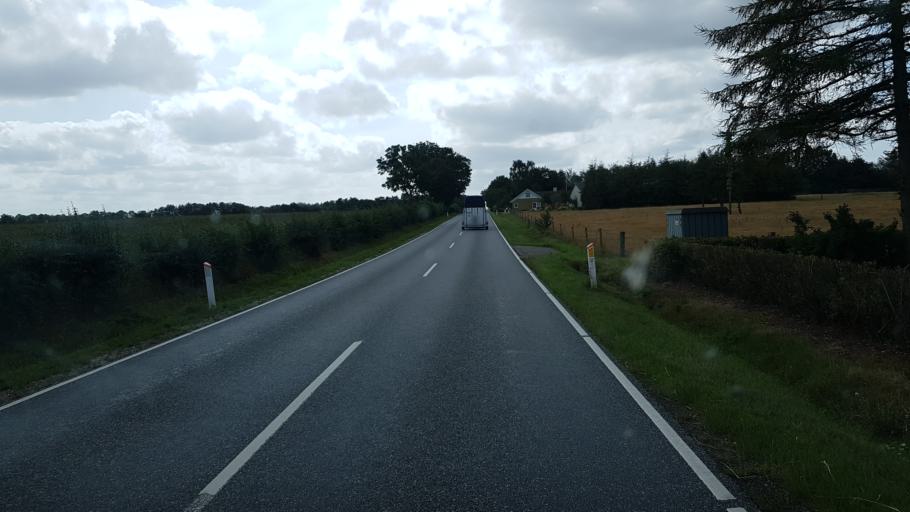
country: DK
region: South Denmark
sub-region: Vejen Kommune
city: Brorup
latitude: 55.5338
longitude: 9.0535
